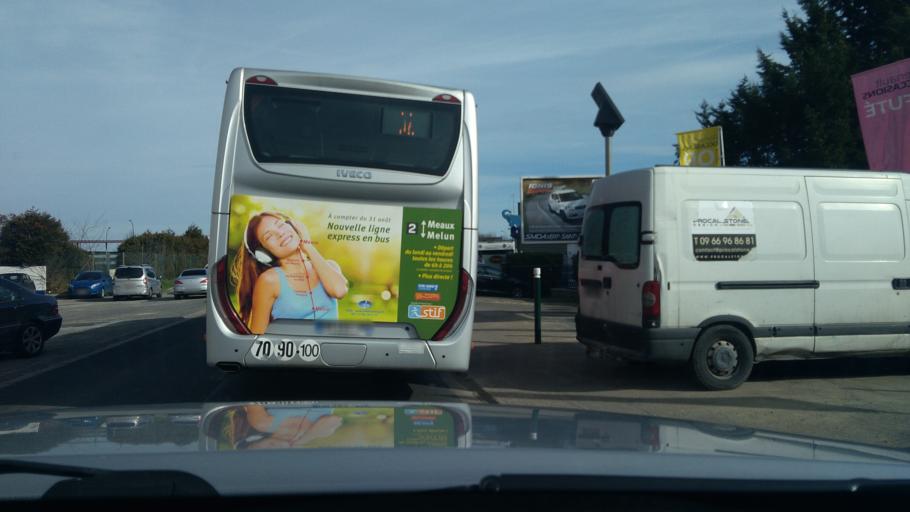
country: FR
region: Ile-de-France
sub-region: Departement de Seine-et-Marne
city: Rubelles
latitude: 48.5413
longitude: 2.6792
